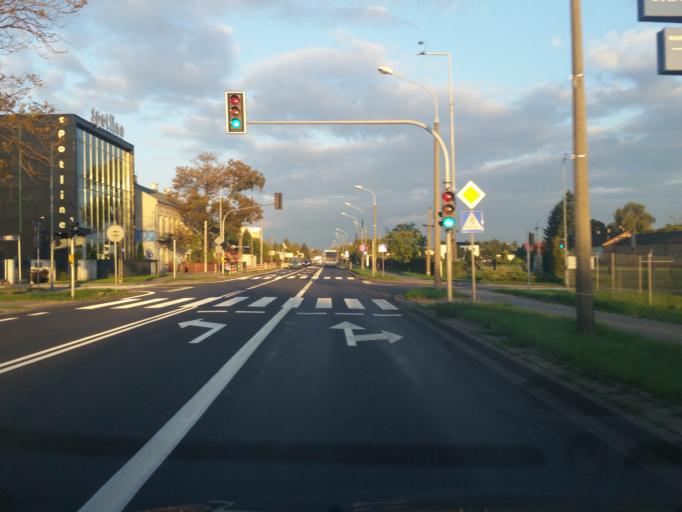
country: PL
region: Masovian Voivodeship
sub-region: Powiat warszawski zachodni
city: Ozarow Mazowiecki
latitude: 52.2109
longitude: 20.7763
